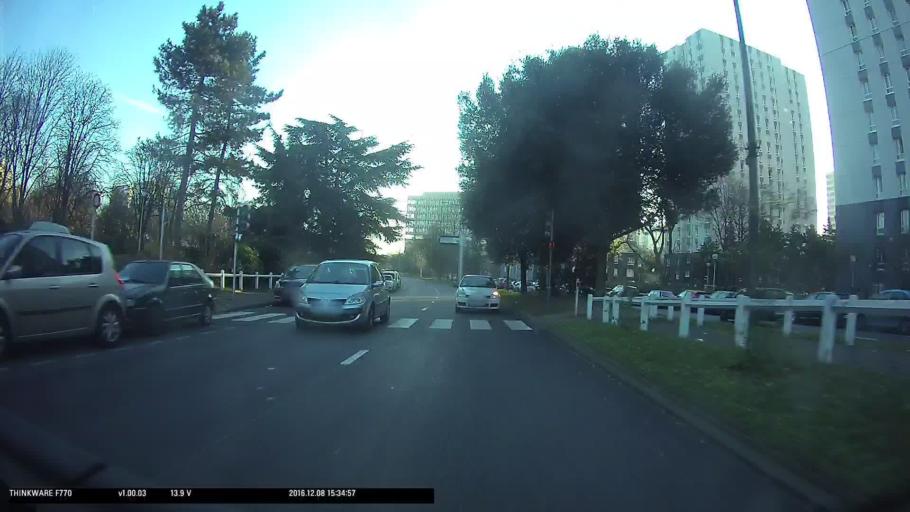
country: FR
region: Ile-de-France
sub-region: Departement de Seine-Saint-Denis
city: Bobigny
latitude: 48.9084
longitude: 2.4458
